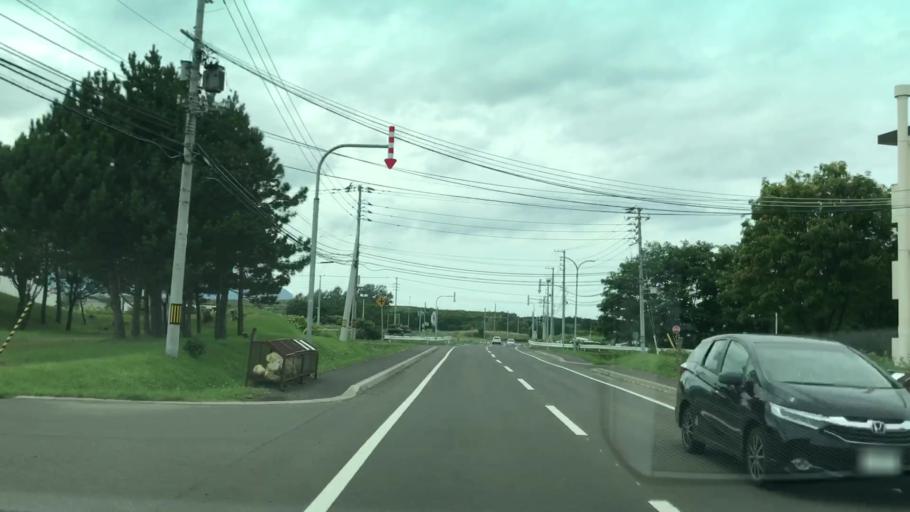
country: JP
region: Hokkaido
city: Iwanai
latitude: 43.0330
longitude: 140.5377
